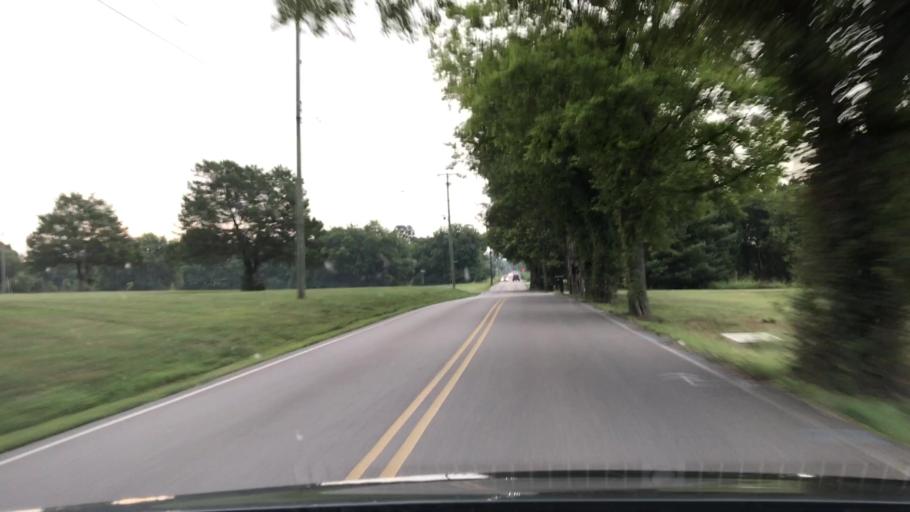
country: US
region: Tennessee
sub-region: Williamson County
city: Nolensville
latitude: 35.9762
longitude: -86.6554
